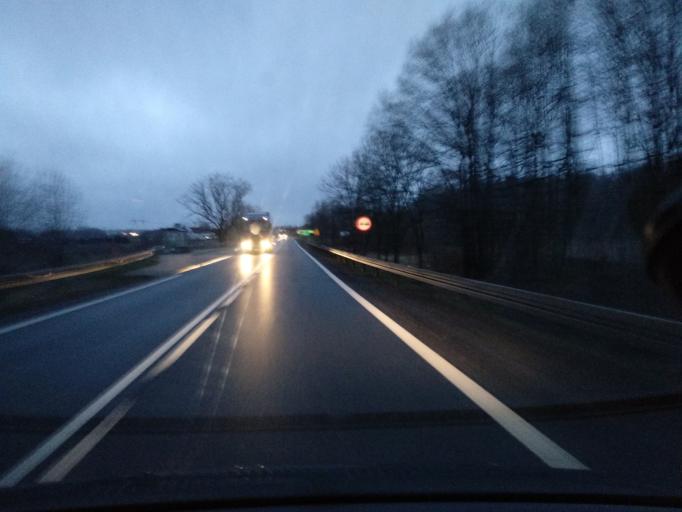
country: PL
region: Lower Silesian Voivodeship
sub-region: Powiat sredzki
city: Malczyce
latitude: 51.1926
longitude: 16.5055
